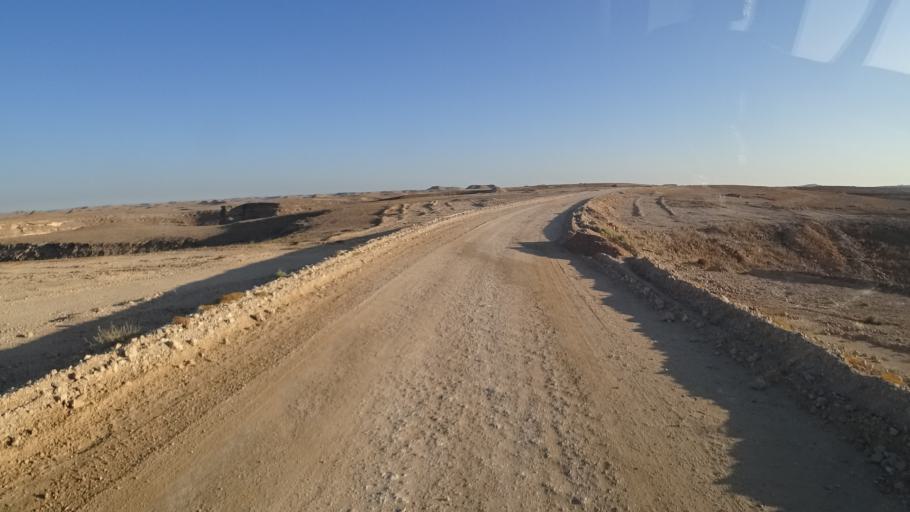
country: YE
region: Al Mahrah
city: Hawf
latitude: 17.1690
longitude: 53.3521
